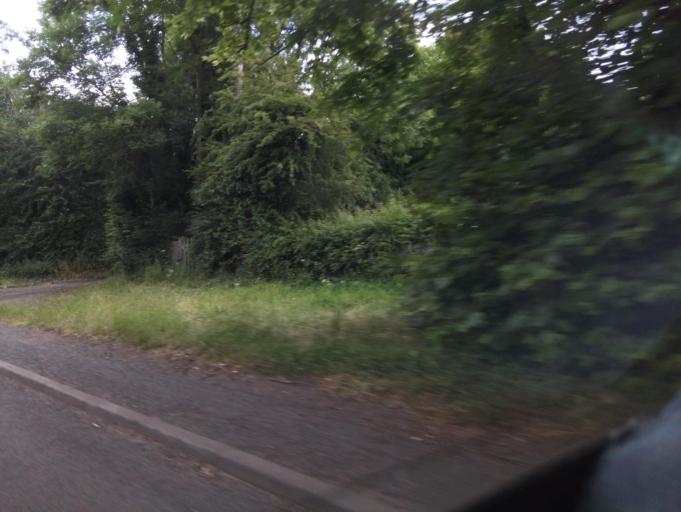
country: GB
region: England
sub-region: Dudley
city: Kingswinford
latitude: 52.4726
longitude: -2.1947
